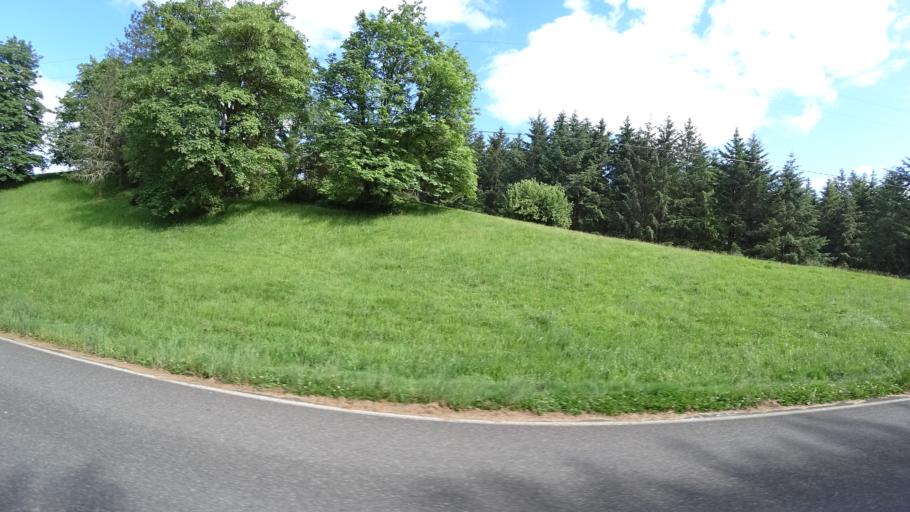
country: US
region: Oregon
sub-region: Washington County
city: Bethany
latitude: 45.6100
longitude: -122.8202
